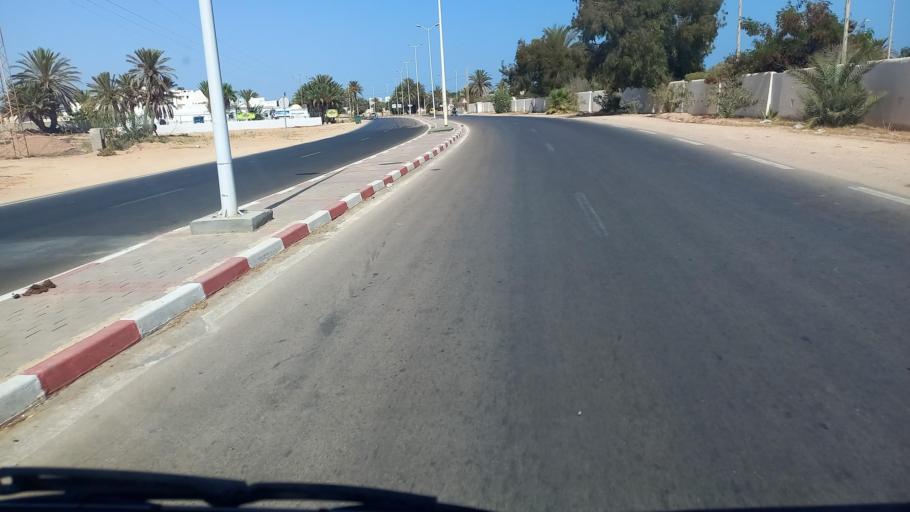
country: TN
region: Madanin
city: Midoun
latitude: 33.8254
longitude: 11.0397
